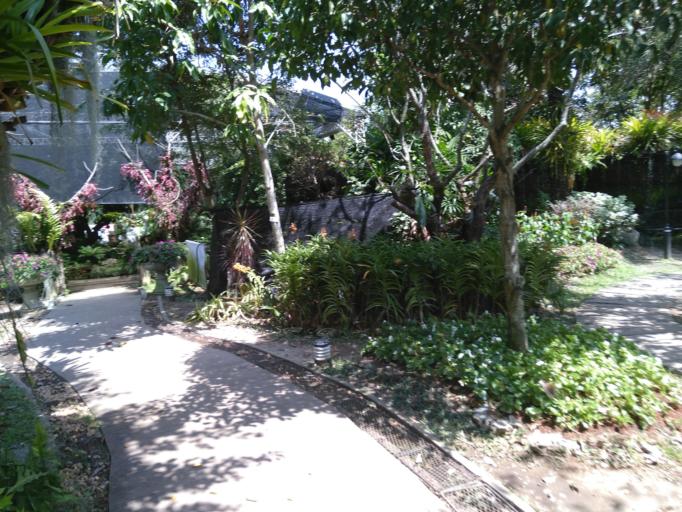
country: TH
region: Chiang Mai
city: Hang Dong
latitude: 18.7501
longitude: 98.9245
